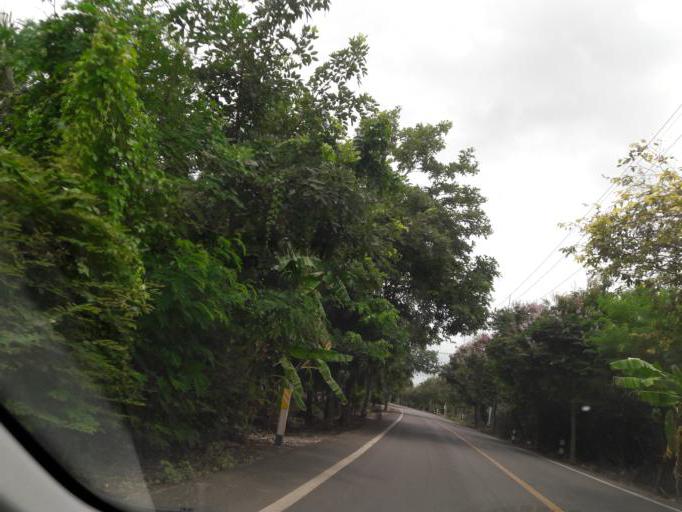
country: TH
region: Samut Sakhon
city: Ban Phaeo
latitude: 13.6133
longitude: 100.0221
